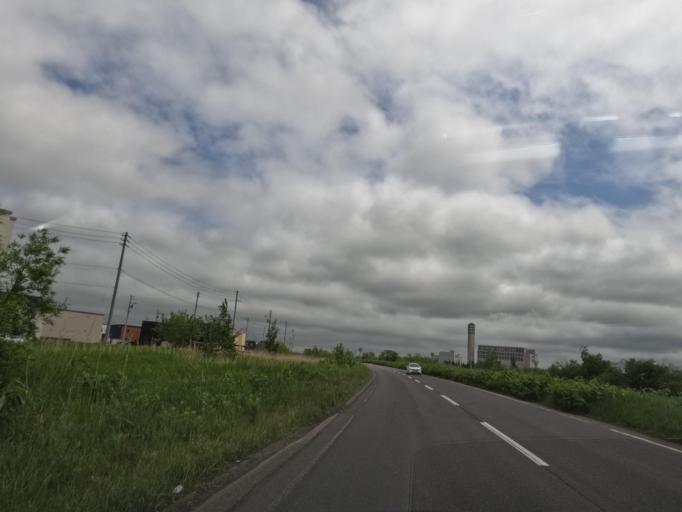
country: JP
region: Hokkaido
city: Sapporo
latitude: 43.0897
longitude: 141.4287
